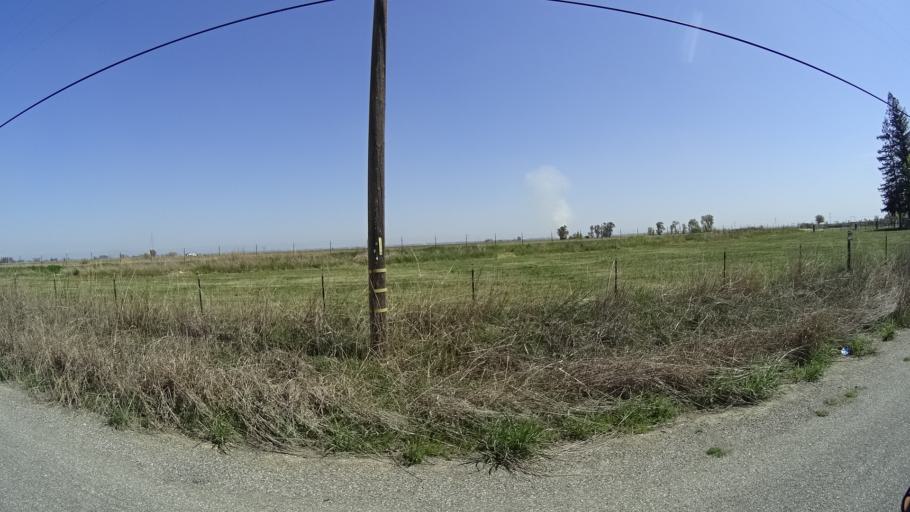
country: US
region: California
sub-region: Glenn County
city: Willows
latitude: 39.5247
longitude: -122.1123
